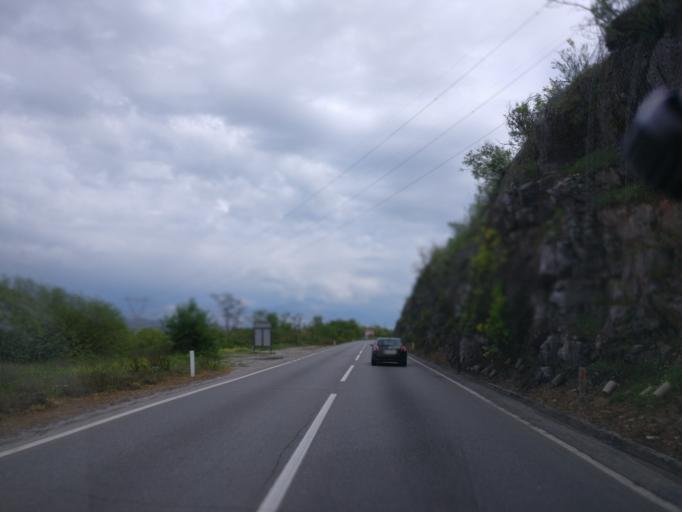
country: ME
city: Spuz
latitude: 42.4550
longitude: 19.1892
